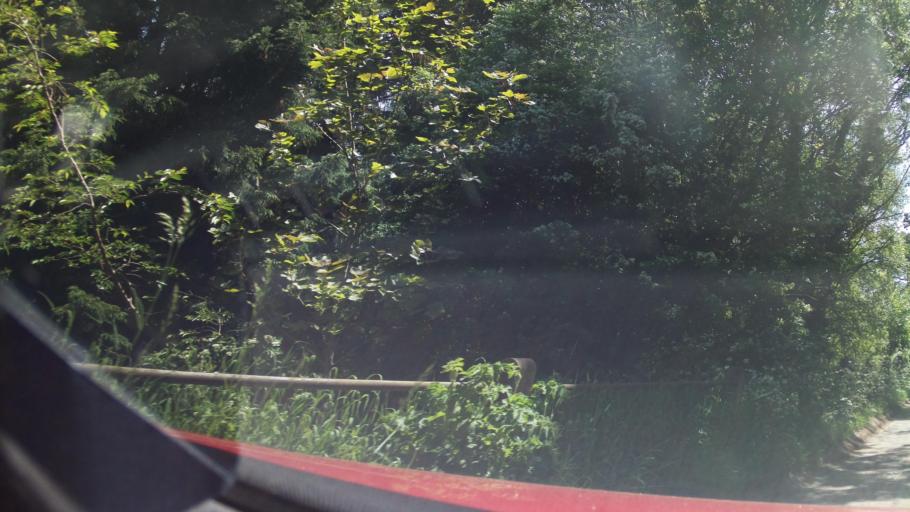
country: GB
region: England
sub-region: Devon
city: Newton Poppleford
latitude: 50.7194
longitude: -3.2826
